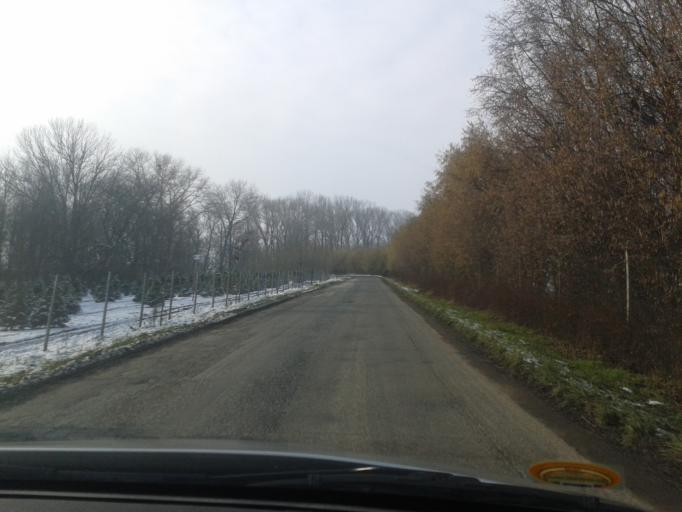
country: CZ
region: Olomoucky
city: Celechovice na Hane
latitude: 49.4969
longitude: 17.0885
